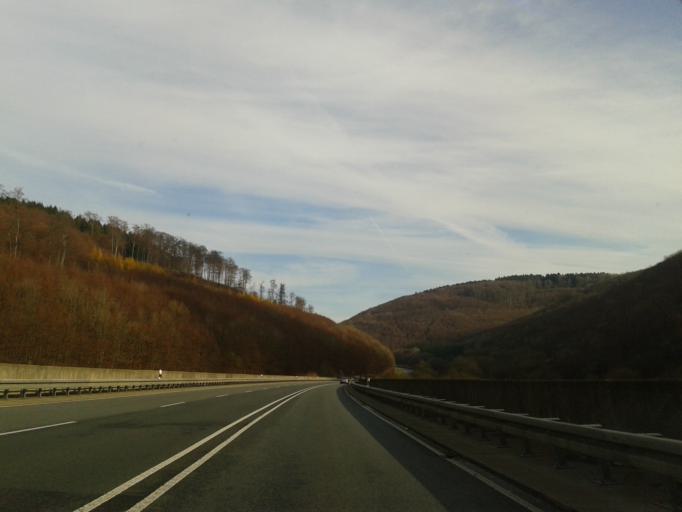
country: DE
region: North Rhine-Westphalia
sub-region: Regierungsbezirk Detmold
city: Schlangen
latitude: 51.8229
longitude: 8.8628
